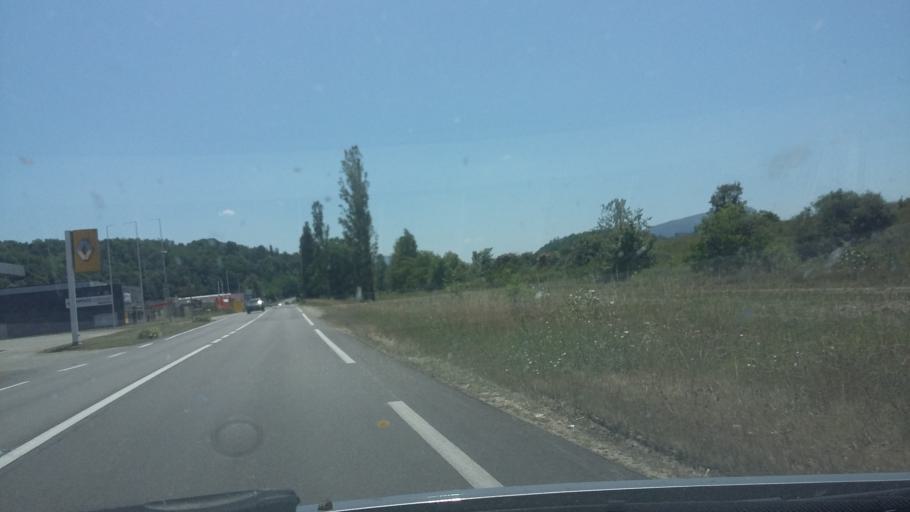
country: FR
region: Rhone-Alpes
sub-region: Departement de l'Ain
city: Belley
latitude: 45.7495
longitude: 5.7072
